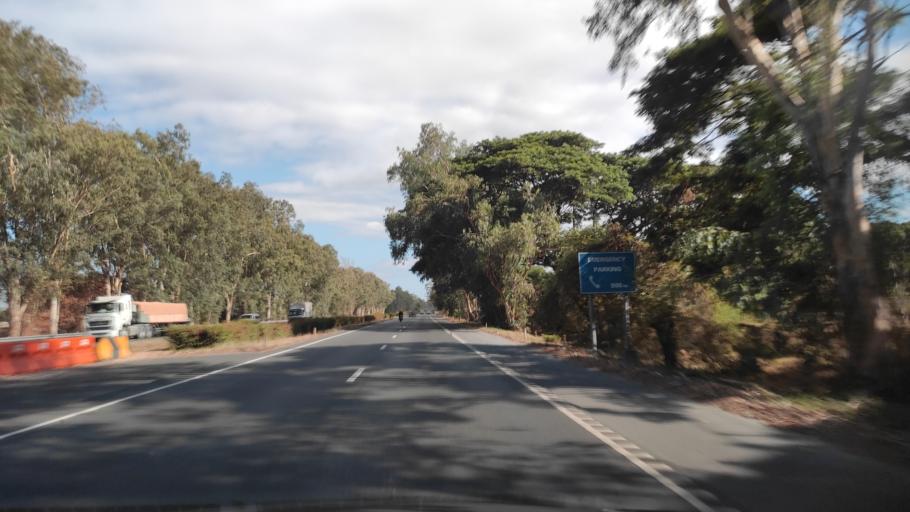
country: PH
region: Central Luzon
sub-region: Province of Pampanga
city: Bulaon
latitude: 15.0732
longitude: 120.6790
